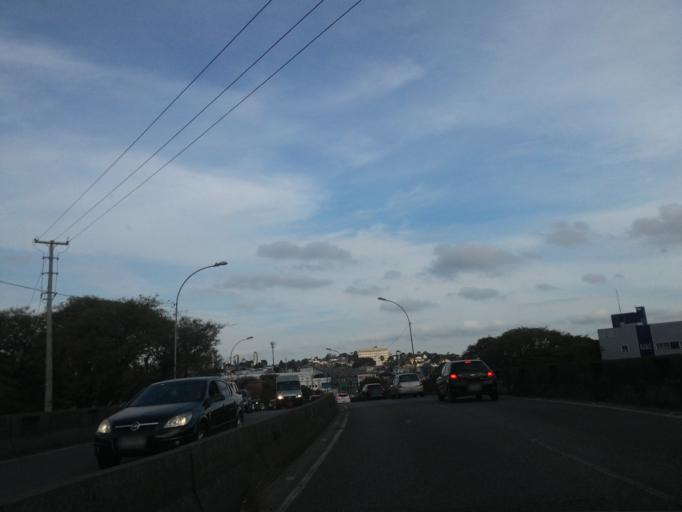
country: BR
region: Parana
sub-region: Curitiba
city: Curitiba
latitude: -25.4407
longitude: -49.2566
